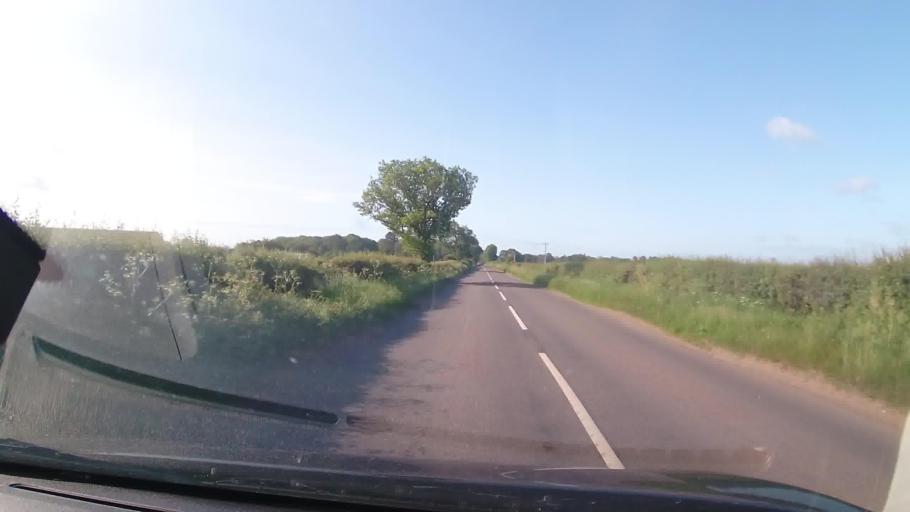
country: GB
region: England
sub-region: Shropshire
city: Shawbury
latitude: 52.8022
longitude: -2.6566
